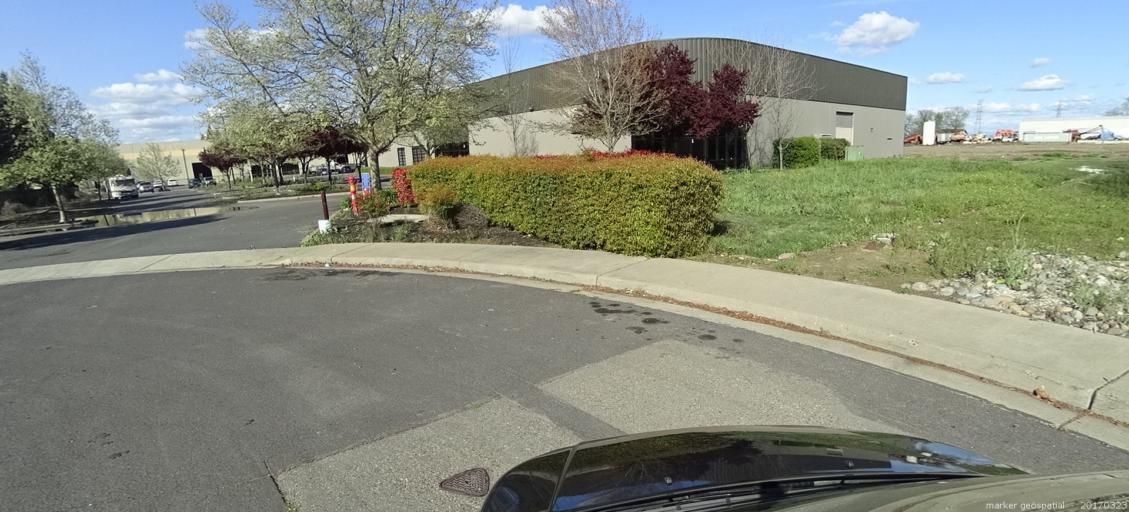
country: US
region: California
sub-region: Sacramento County
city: Rosemont
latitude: 38.5164
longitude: -121.3679
